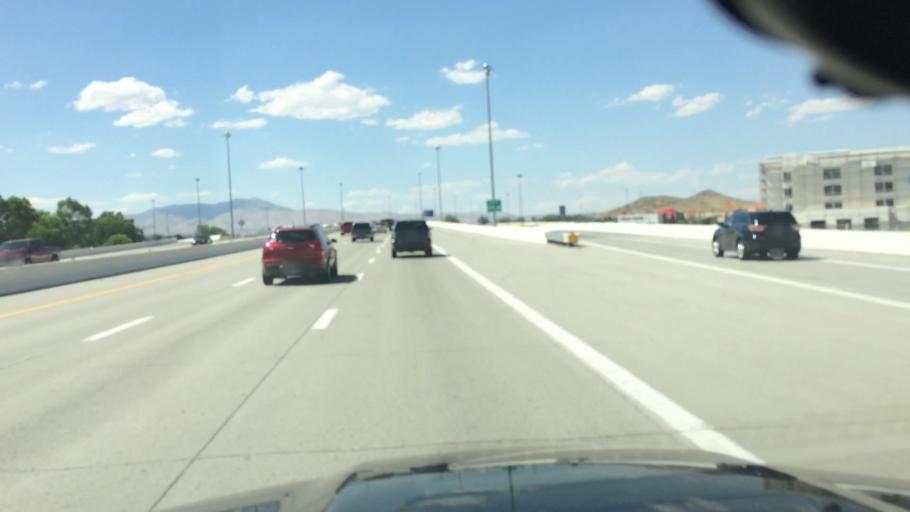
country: US
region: Nevada
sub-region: Washoe County
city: Sparks
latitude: 39.4355
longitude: -119.7625
